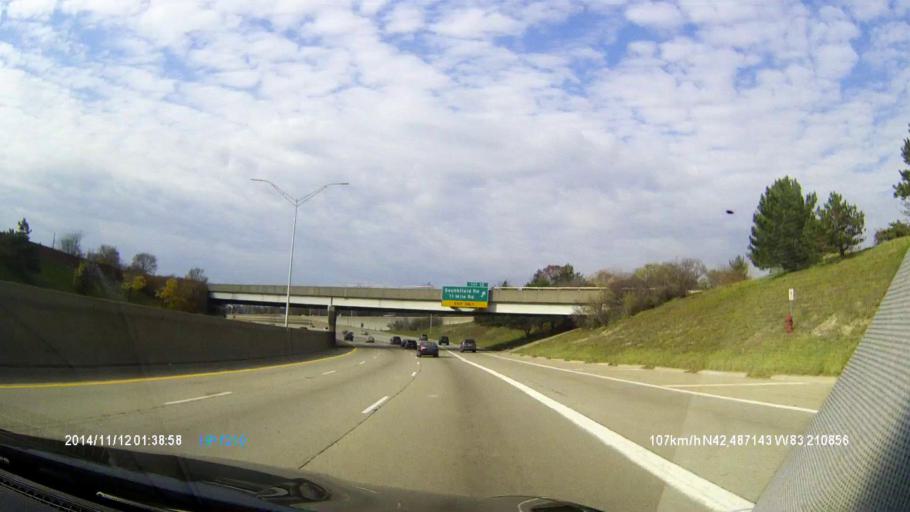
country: US
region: Michigan
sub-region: Oakland County
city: Lathrup Village
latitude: 42.4872
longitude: -83.2110
